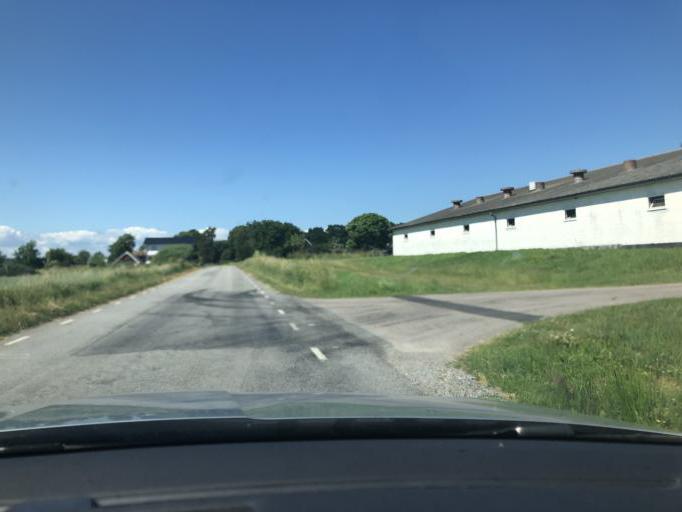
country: SE
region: Blekinge
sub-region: Karlshamns Kommun
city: Morrum
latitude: 56.1470
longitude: 14.6417
